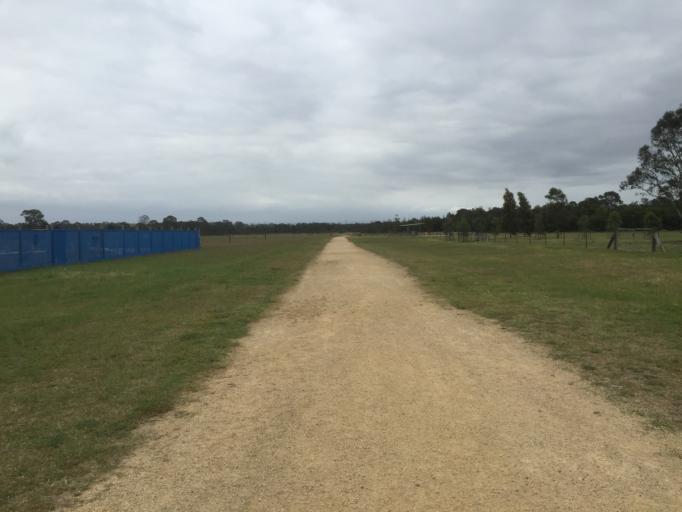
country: AU
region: New South Wales
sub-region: Blacktown
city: Doonside
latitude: -33.7850
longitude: 150.8711
